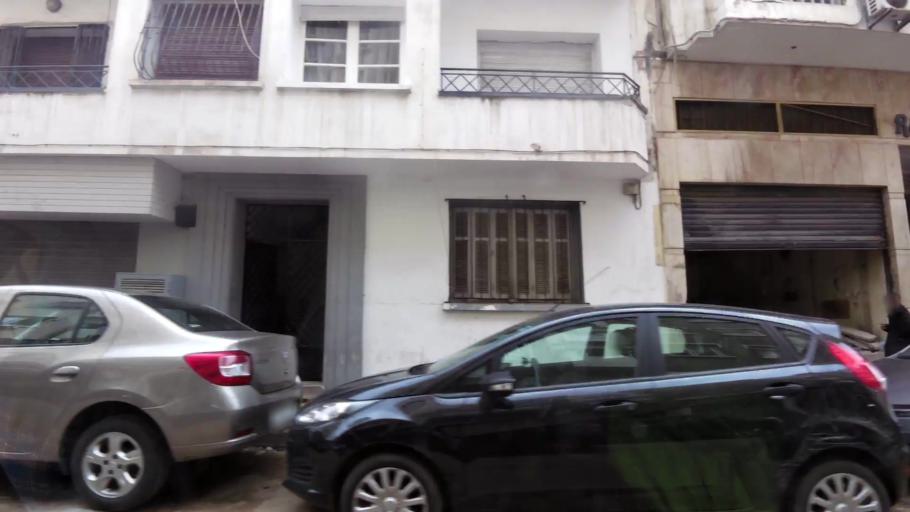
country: MA
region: Grand Casablanca
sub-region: Casablanca
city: Casablanca
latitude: 33.5936
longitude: -7.6325
